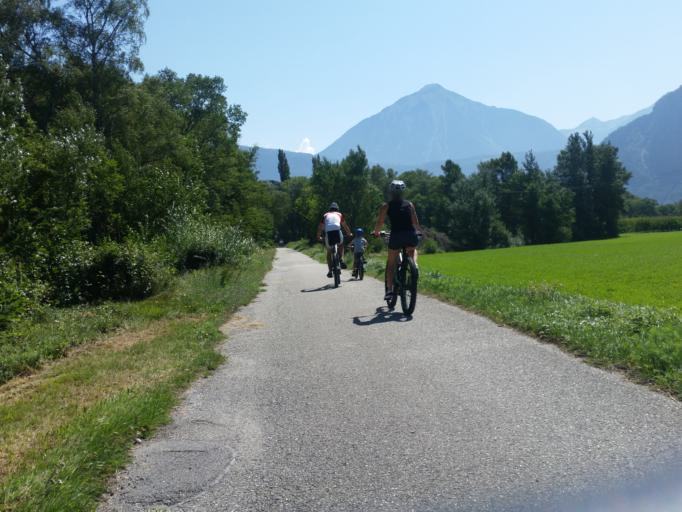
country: CH
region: Valais
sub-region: Saint-Maurice District
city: Vernayaz
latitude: 46.1386
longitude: 7.0498
